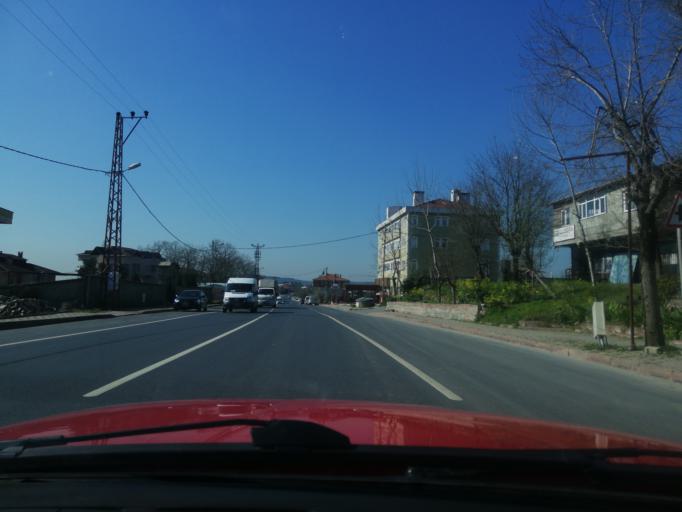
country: TR
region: Istanbul
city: Umraniye
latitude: 41.0690
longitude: 29.1638
